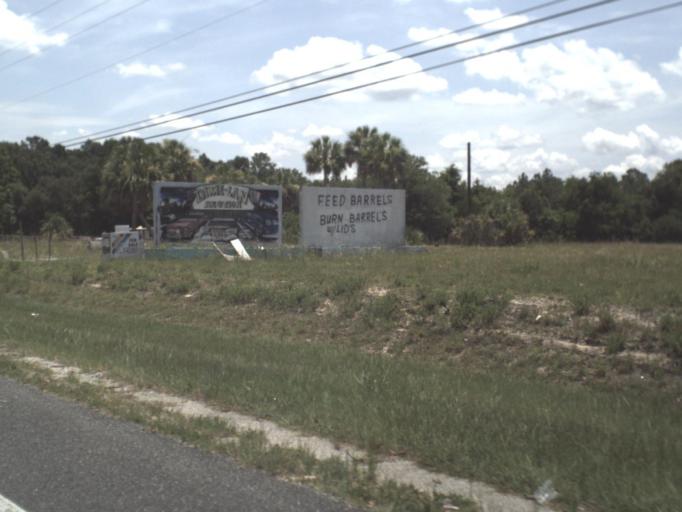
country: US
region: Florida
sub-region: Dixie County
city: Cross City
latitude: 29.6081
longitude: -83.0651
